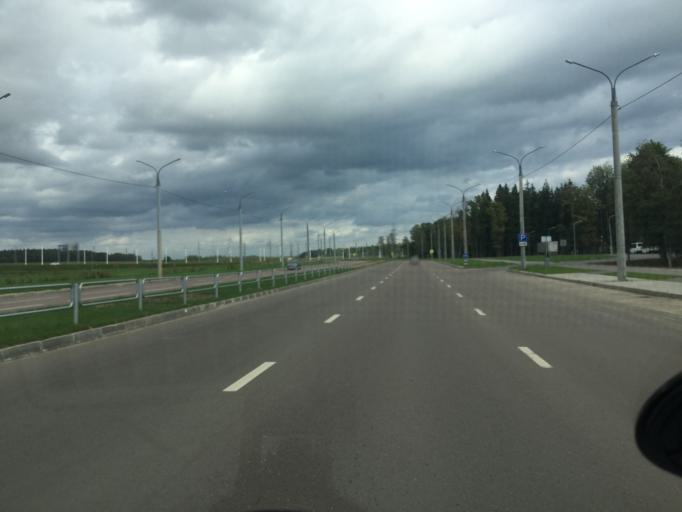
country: BY
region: Vitebsk
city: Vitebsk
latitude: 55.1670
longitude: 30.2922
